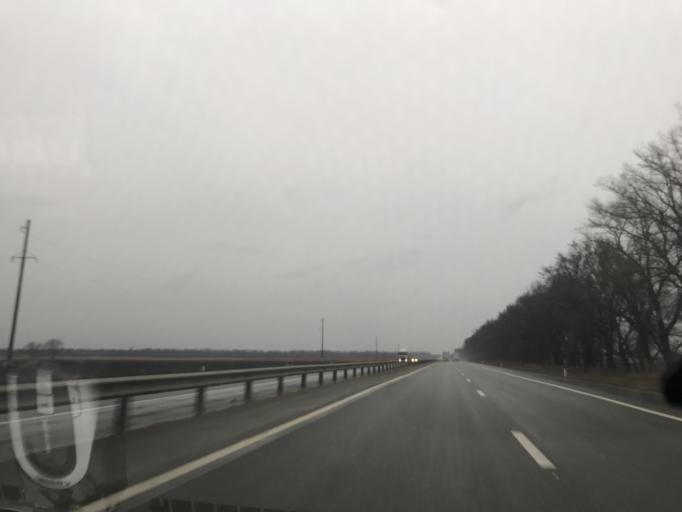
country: RU
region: Krasnodarskiy
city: Kislyakovskaya
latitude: 46.3836
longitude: 39.7436
